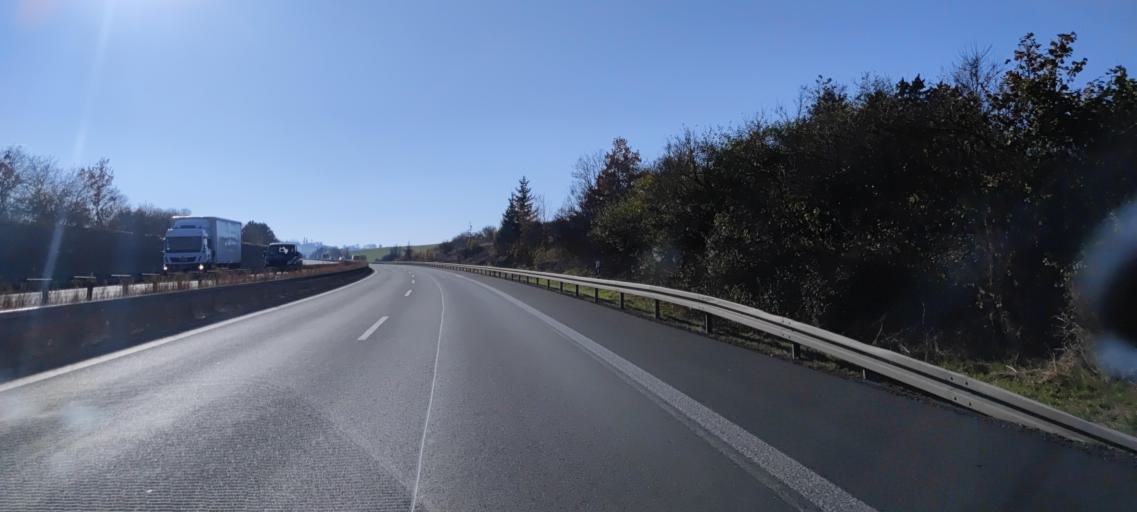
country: DE
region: Saxony
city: Weischlitz
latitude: 50.4248
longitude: 12.0621
